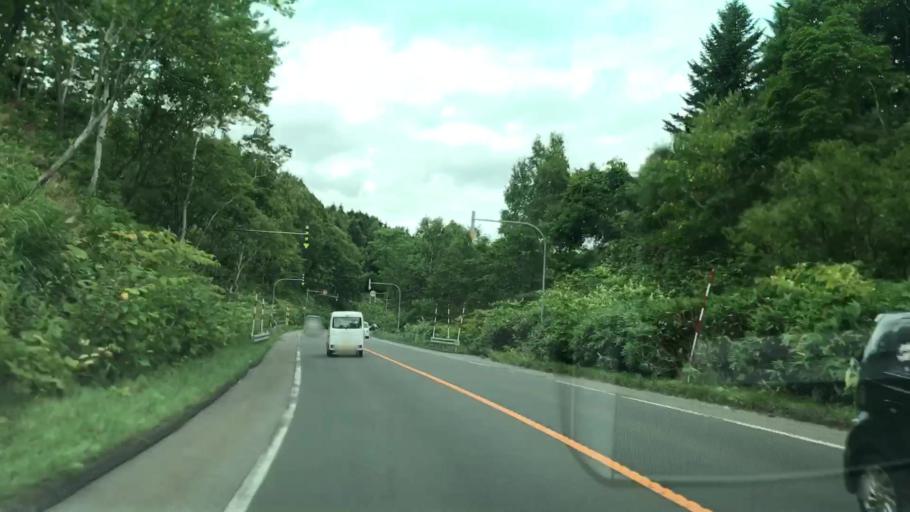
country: JP
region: Hokkaido
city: Niseko Town
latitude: 42.9274
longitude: 140.7164
